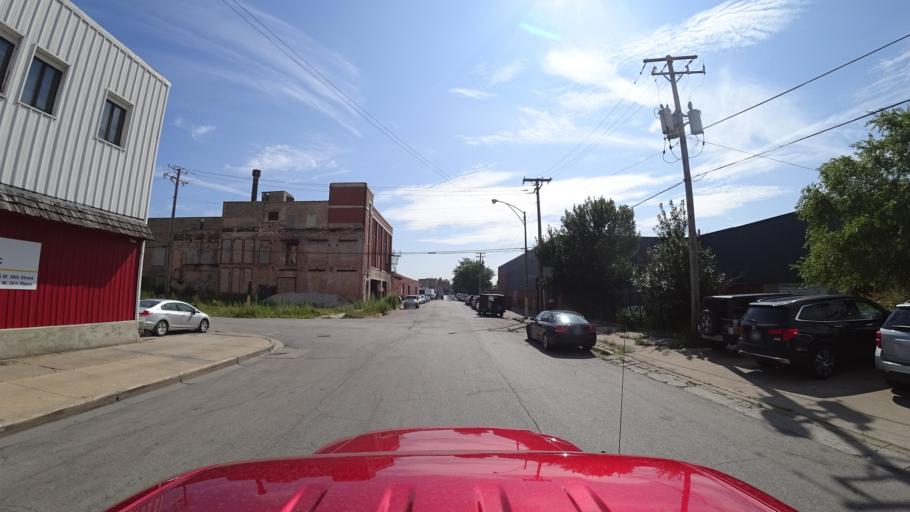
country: US
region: Illinois
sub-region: Cook County
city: Chicago
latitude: 41.8245
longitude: -87.6496
